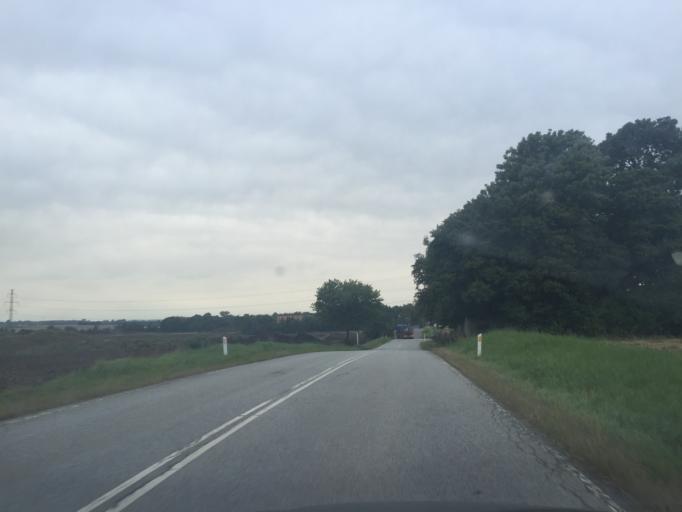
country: DK
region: Capital Region
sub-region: Hoje-Taastrup Kommune
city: Flong
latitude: 55.6732
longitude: 12.2102
